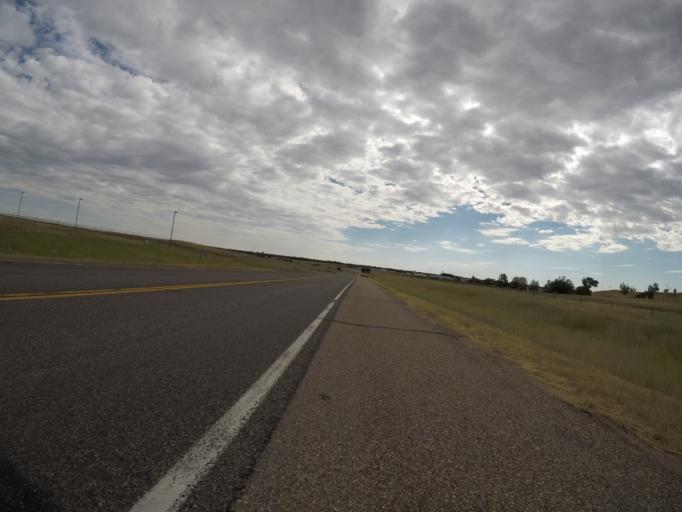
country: US
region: Wyoming
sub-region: Laramie County
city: Cheyenne
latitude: 41.1344
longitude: -104.8524
